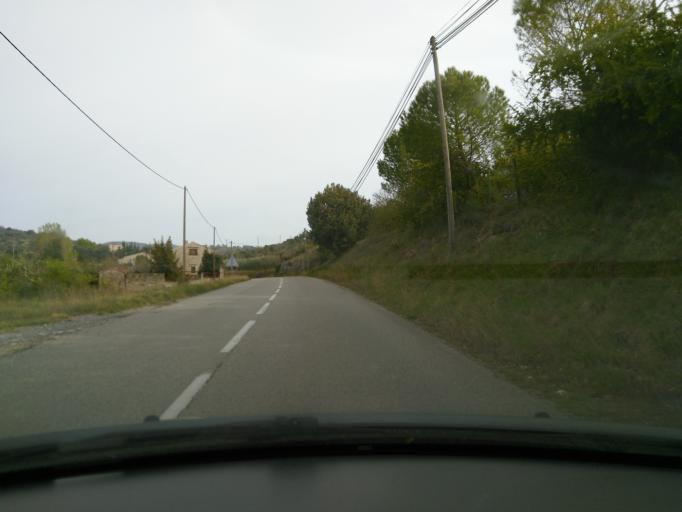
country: FR
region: Rhone-Alpes
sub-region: Departement de l'Ardeche
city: Ruoms
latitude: 44.4530
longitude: 4.4153
